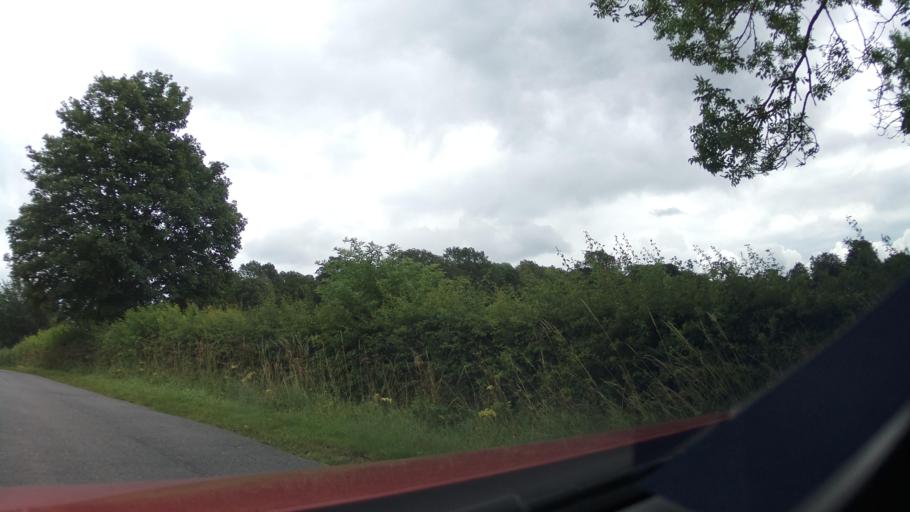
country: GB
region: England
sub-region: District of Rutland
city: Morcott
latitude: 52.5248
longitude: -0.5931
